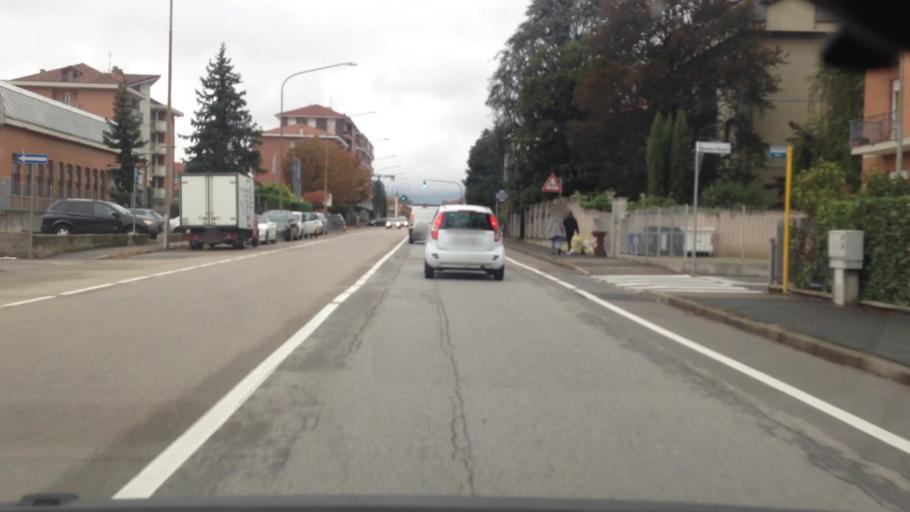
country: IT
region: Piedmont
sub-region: Provincia di Torino
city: Chieri
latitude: 45.0035
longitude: 7.8403
